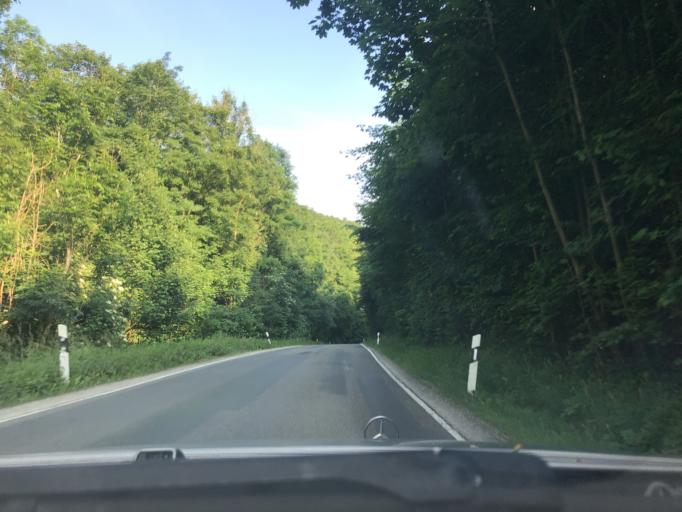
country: DE
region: Thuringia
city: Kleinbartloff
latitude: 51.3417
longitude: 10.3703
